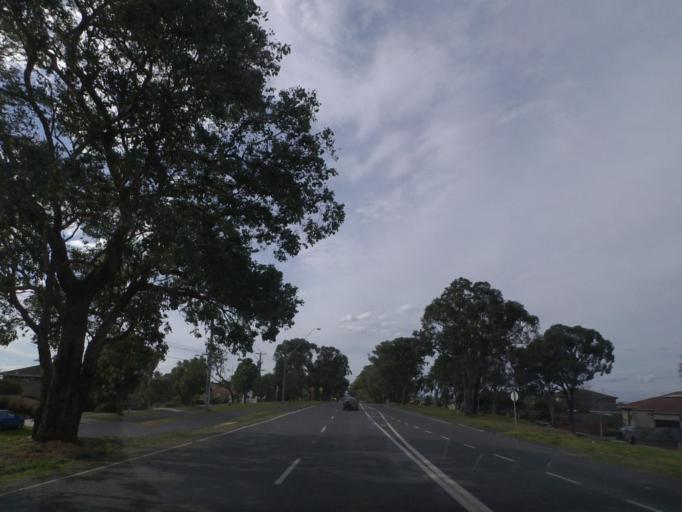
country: AU
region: Victoria
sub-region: Manningham
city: Donvale
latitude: -37.7691
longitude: 145.1710
